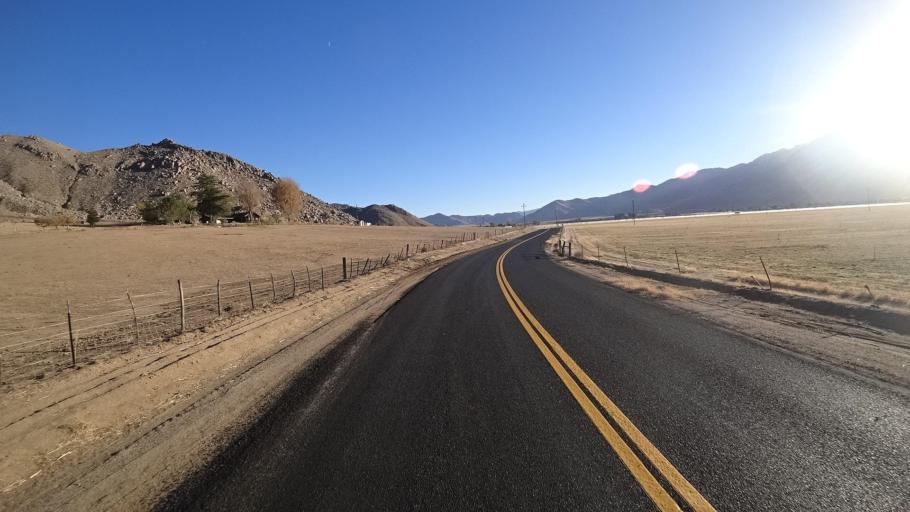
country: US
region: California
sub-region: Kern County
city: Weldon
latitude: 35.6629
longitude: -118.2573
